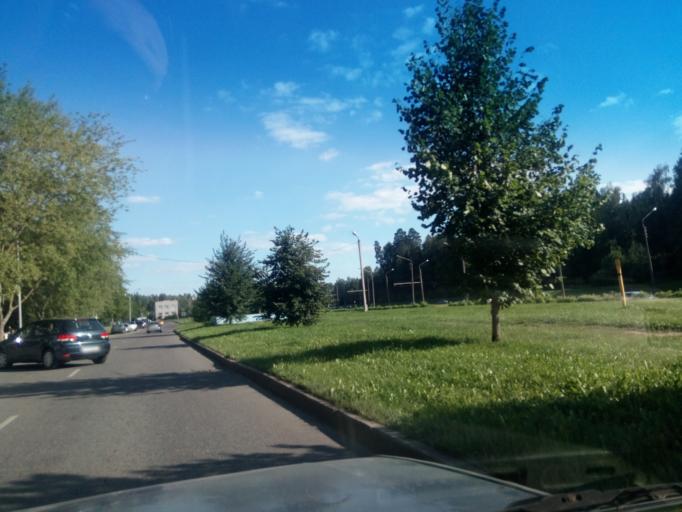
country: BY
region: Vitebsk
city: Navapolatsk
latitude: 55.5209
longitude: 28.6657
